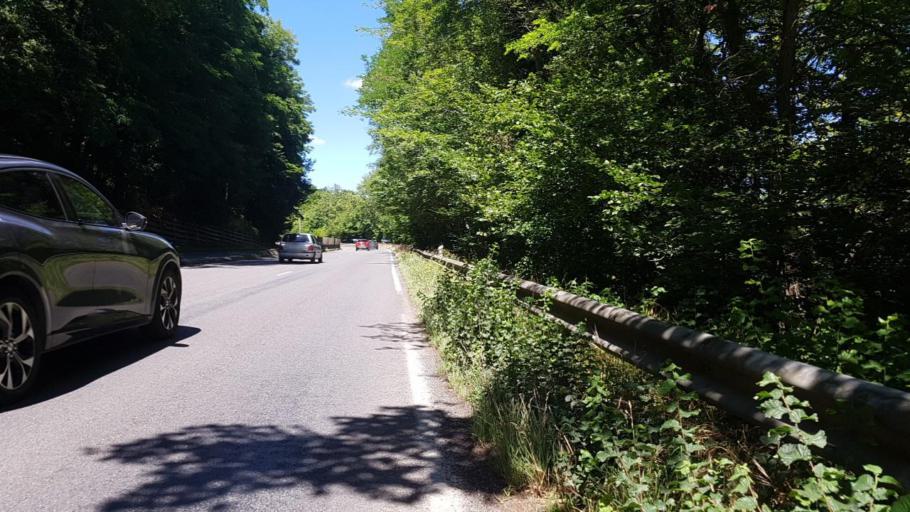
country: FR
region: Ile-de-France
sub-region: Departement de Seine-et-Marne
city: Saint-Jean-les-Deux-Jumeaux
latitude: 48.9579
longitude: 3.0032
